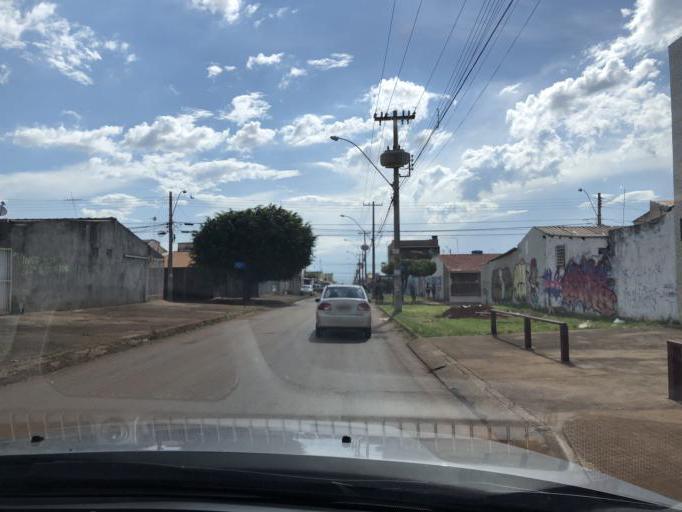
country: BR
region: Federal District
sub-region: Brasilia
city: Brasilia
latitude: -15.7940
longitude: -48.1222
